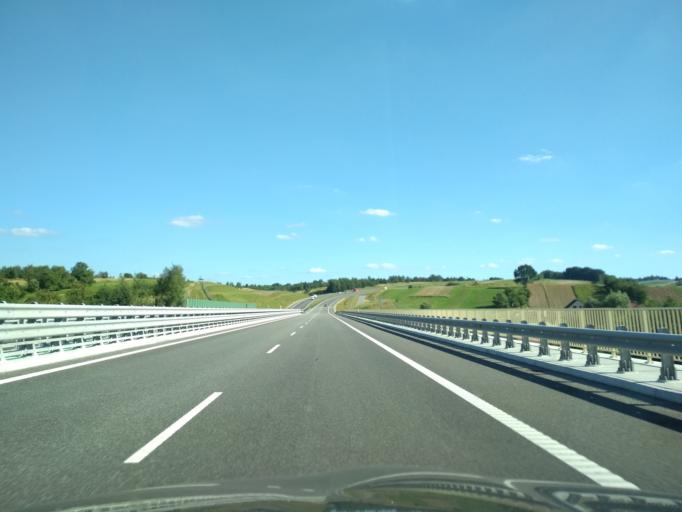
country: PL
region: Subcarpathian Voivodeship
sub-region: Rzeszow
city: Przybyszowka
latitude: 50.0474
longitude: 21.9300
